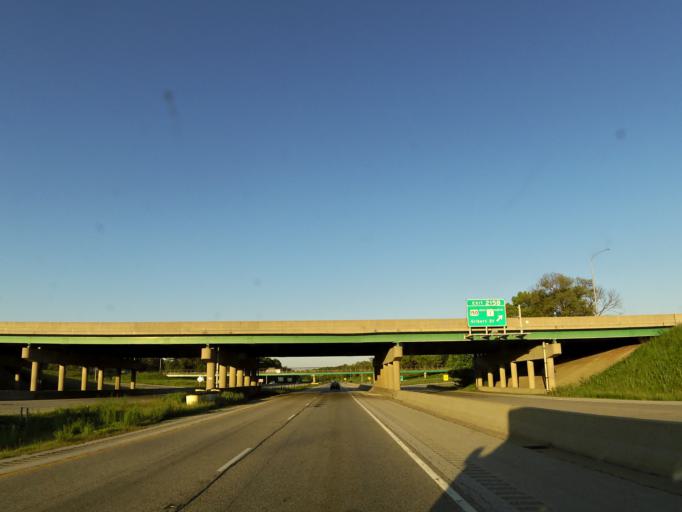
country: US
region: Illinois
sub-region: Vermilion County
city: Tilton
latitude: 40.1049
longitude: -87.6367
